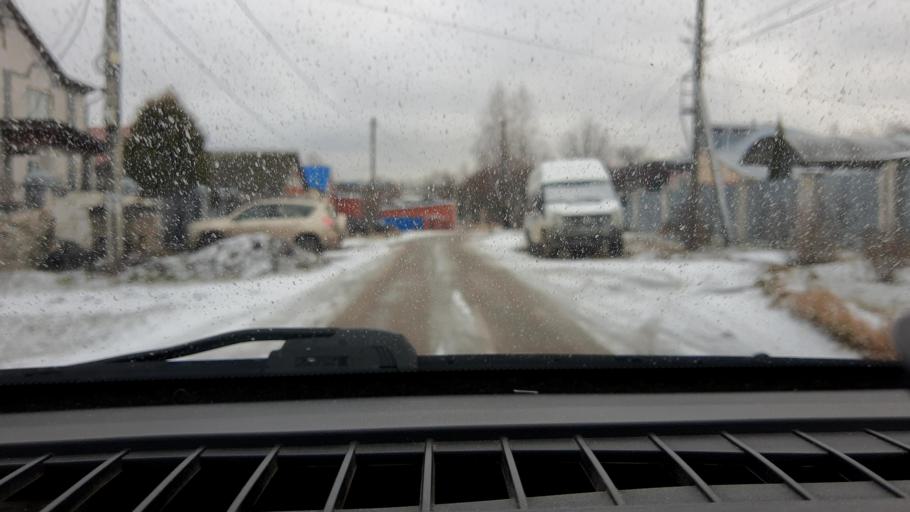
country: RU
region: Nizjnij Novgorod
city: Taremskoye
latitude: 55.9414
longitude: 43.0594
